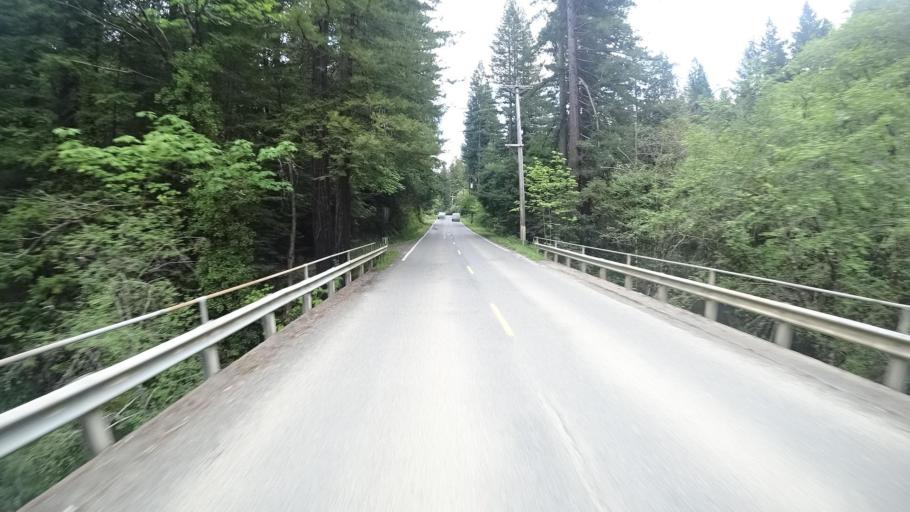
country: US
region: California
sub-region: Humboldt County
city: Redway
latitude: 40.1272
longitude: -123.8526
